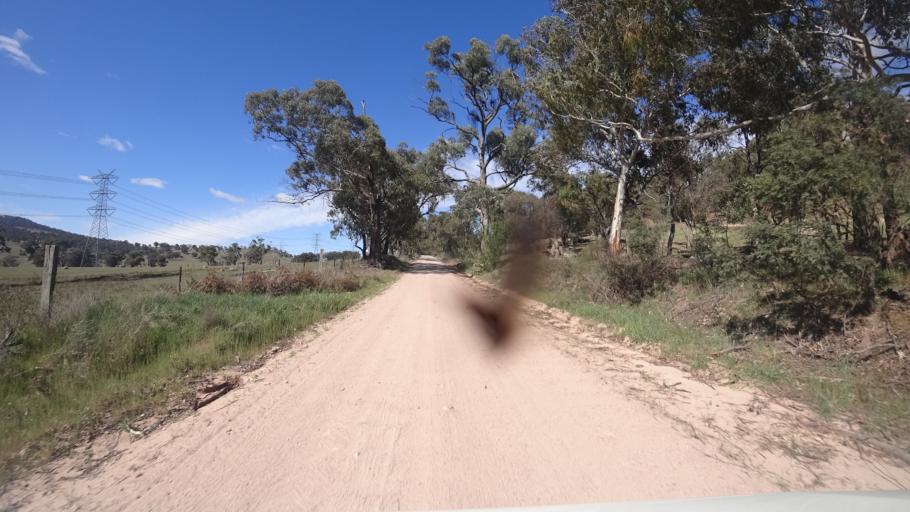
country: AU
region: New South Wales
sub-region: Lithgow
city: Portland
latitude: -33.5297
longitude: 149.9344
